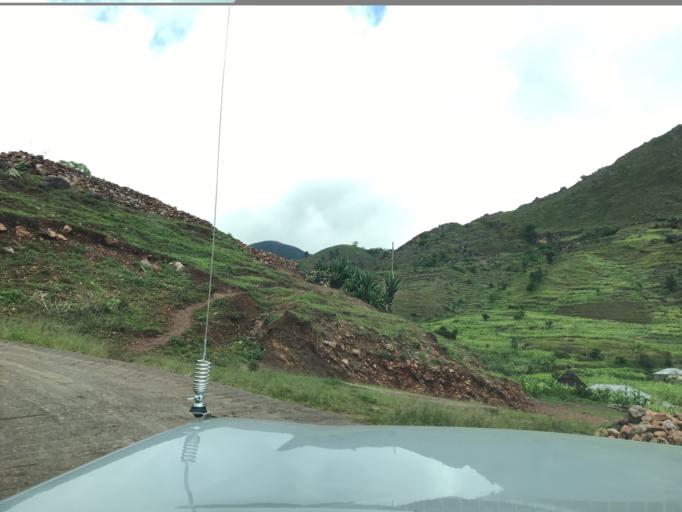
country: TL
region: Aileu
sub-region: Aileu Villa
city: Aileu
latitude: -8.8603
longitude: 125.5718
